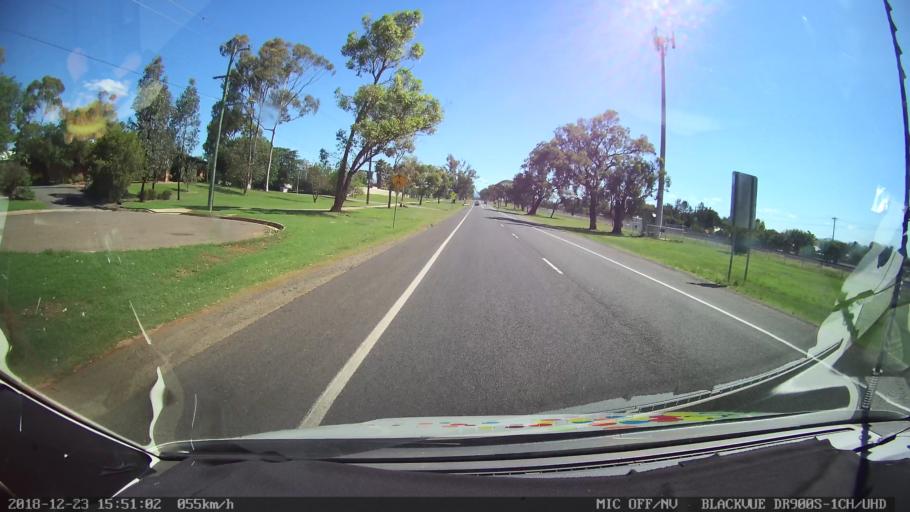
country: AU
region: New South Wales
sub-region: Tamworth Municipality
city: South Tamworth
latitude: -31.1097
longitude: 150.8982
